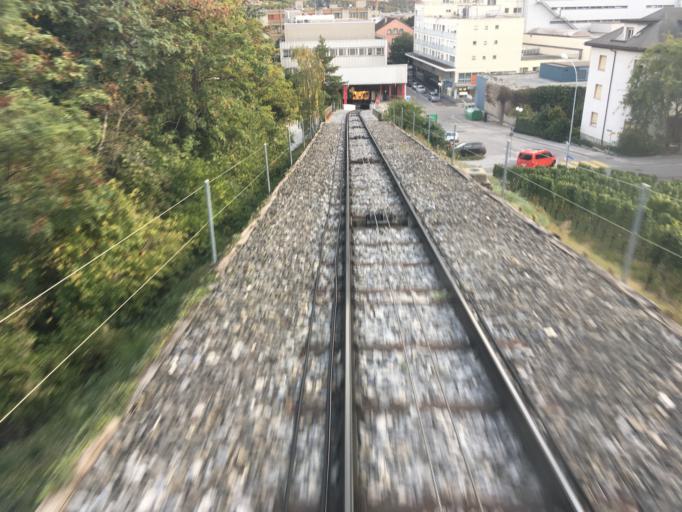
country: CH
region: Valais
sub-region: Sierre District
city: Sierre
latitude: 46.2937
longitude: 7.5297
